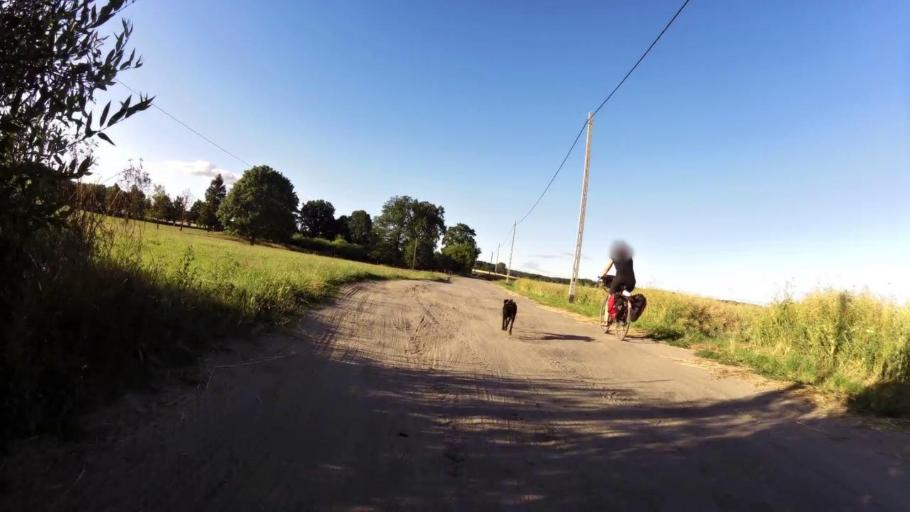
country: PL
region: West Pomeranian Voivodeship
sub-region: Powiat swidwinski
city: Swidwin
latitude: 53.7363
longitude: 15.8587
